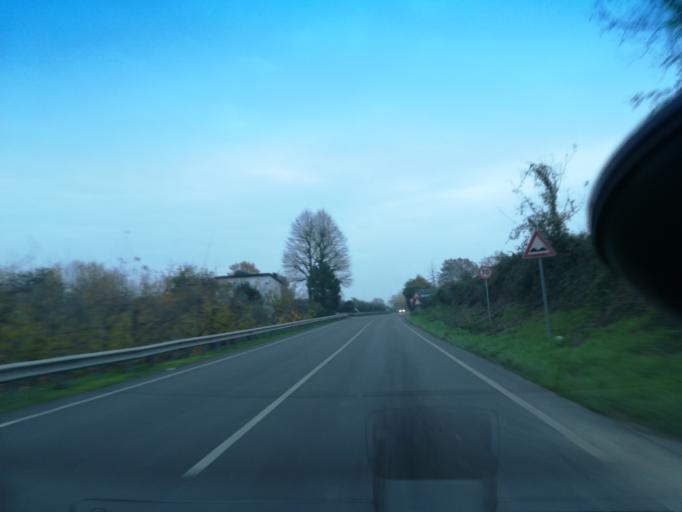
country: IT
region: Emilia-Romagna
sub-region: Provincia di Ravenna
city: Castel Bolognese
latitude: 44.3330
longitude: 11.7658
